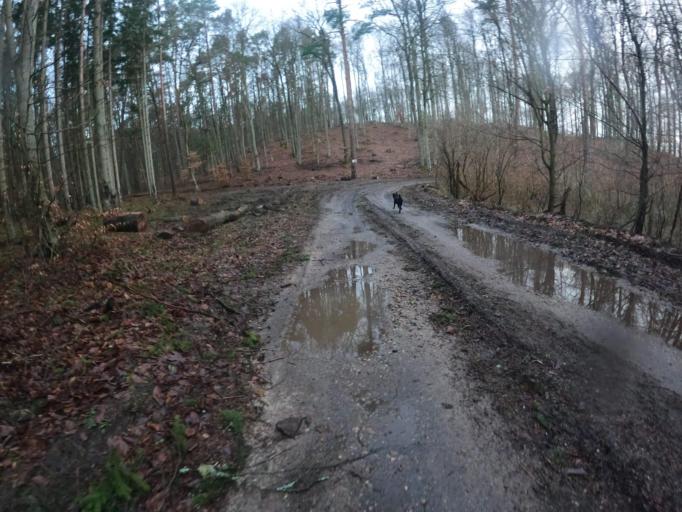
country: PL
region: West Pomeranian Voivodeship
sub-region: Powiat slawienski
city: Slawno
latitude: 54.2832
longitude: 16.7182
